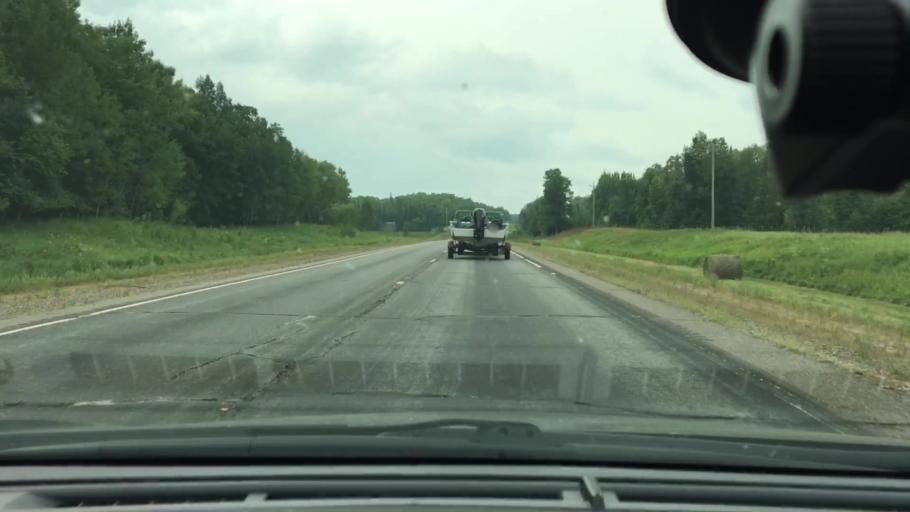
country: US
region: Minnesota
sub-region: Crow Wing County
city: Crosby
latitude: 46.6261
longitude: -93.9464
